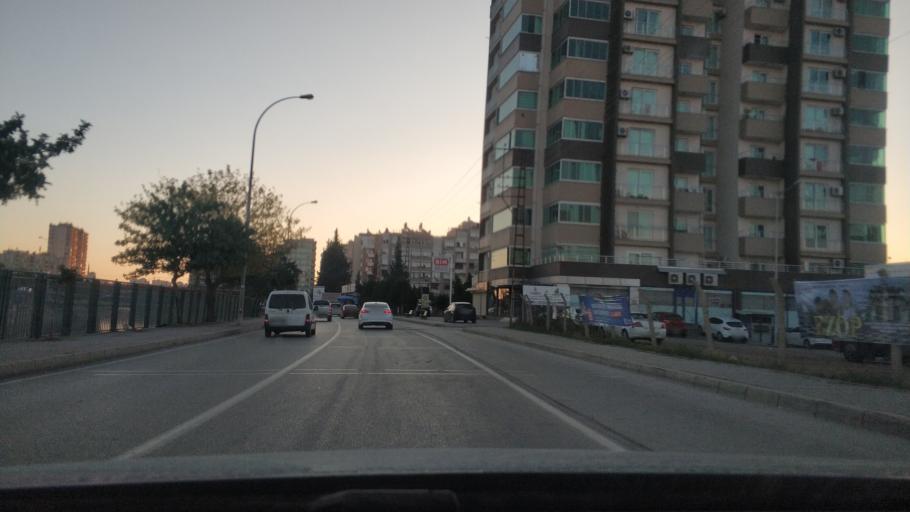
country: TR
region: Adana
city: Seyhan
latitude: 37.0104
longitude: 35.2997
